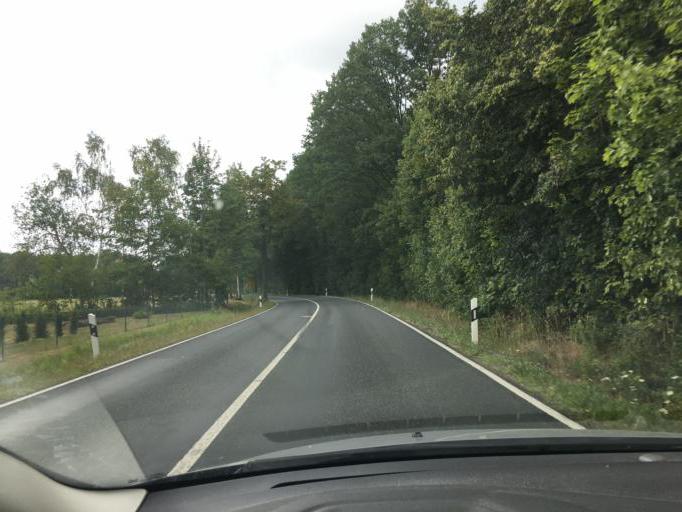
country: DE
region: Saxony
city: Kitzscher
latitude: 51.1213
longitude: 12.5678
